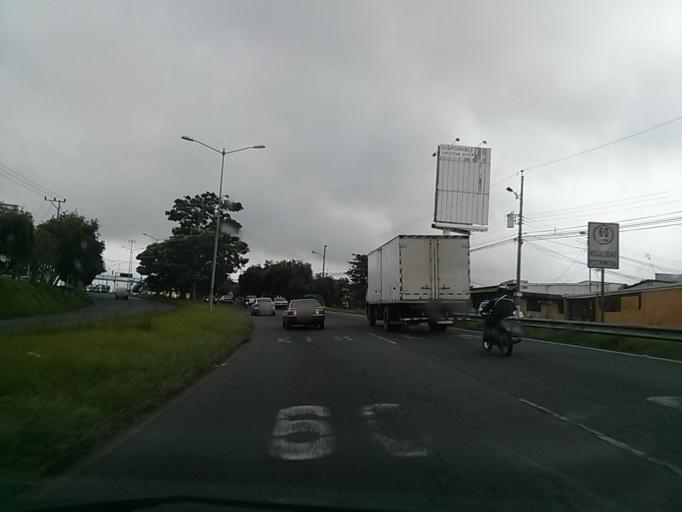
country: CR
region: San Jose
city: San Felipe
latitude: 9.9134
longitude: -84.1052
